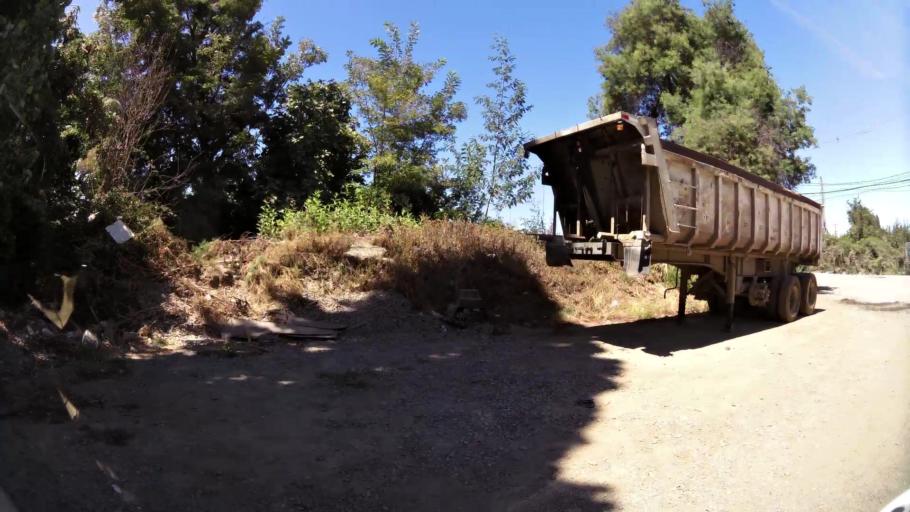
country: CL
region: O'Higgins
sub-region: Provincia de Cachapoal
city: Rancagua
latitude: -34.1536
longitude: -70.7493
